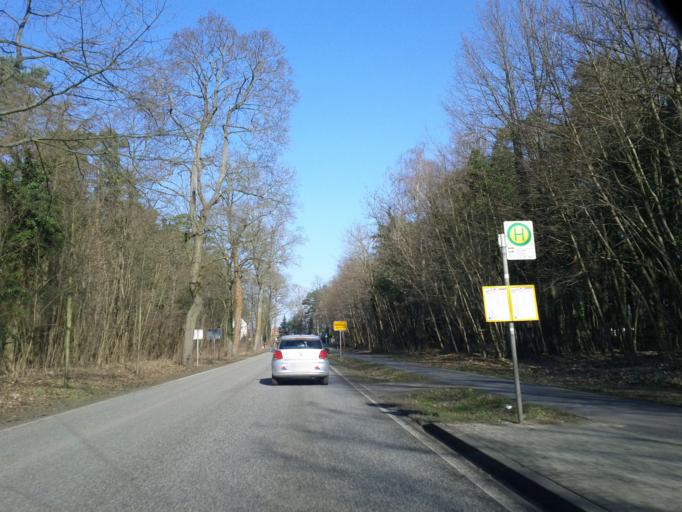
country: DE
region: Brandenburg
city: Woltersdorf
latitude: 52.4411
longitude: 13.7563
